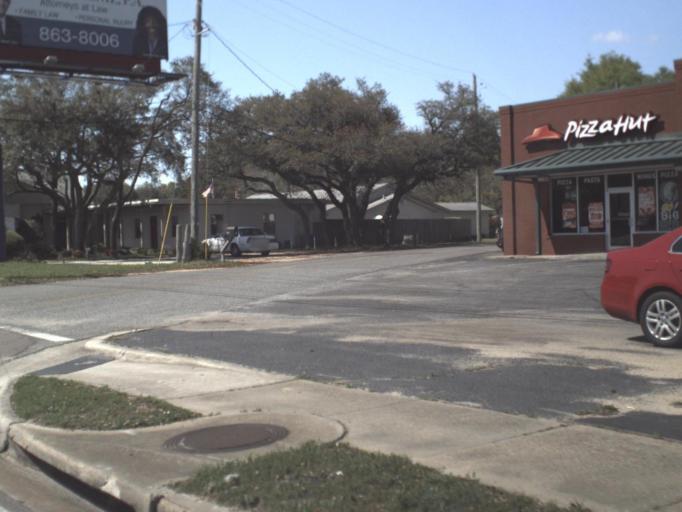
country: US
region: Florida
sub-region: Okaloosa County
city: Ocean City
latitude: 30.4421
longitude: -86.5995
